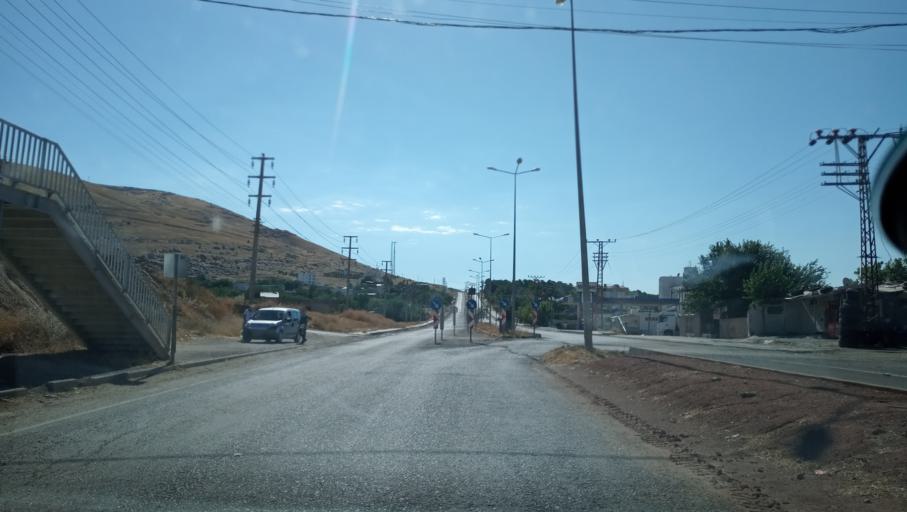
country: TR
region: Diyarbakir
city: Silvan
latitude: 38.1350
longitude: 41.0324
